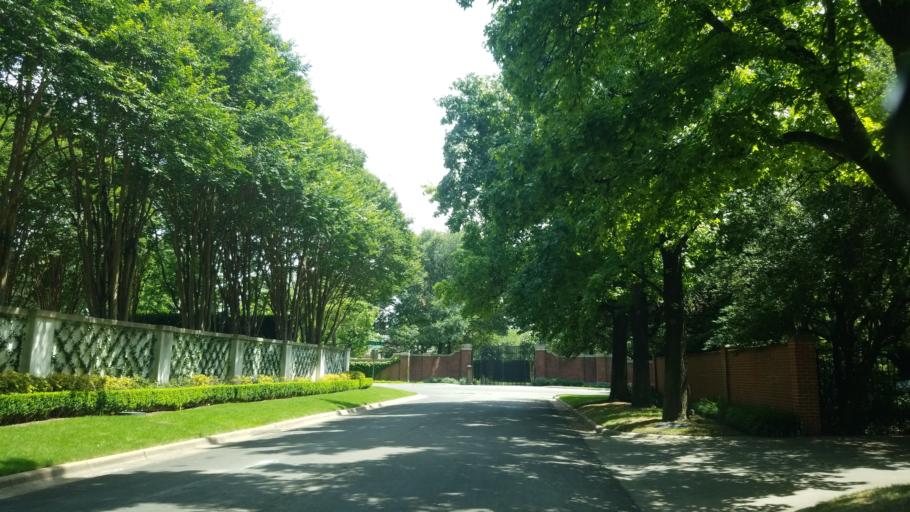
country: US
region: Texas
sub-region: Dallas County
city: University Park
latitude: 32.8712
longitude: -96.8055
